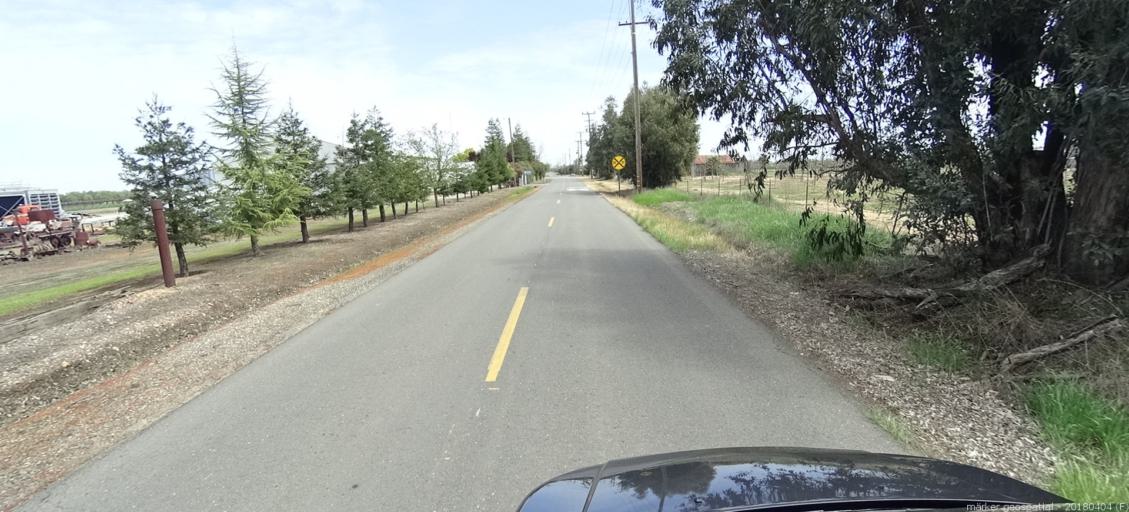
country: US
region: California
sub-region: Sacramento County
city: Herald
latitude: 38.3027
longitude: -121.2472
